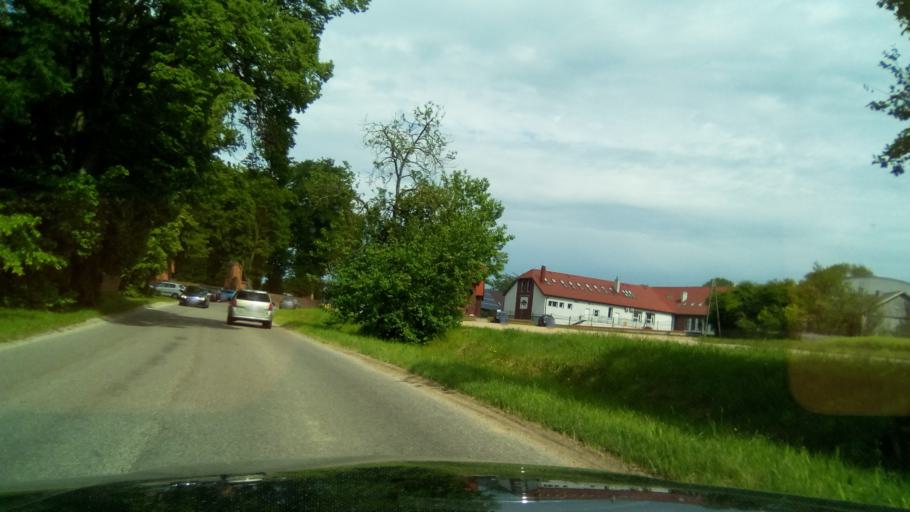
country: PL
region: Pomeranian Voivodeship
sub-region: Powiat pucki
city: Wierzchucino
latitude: 54.7871
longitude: 18.0804
